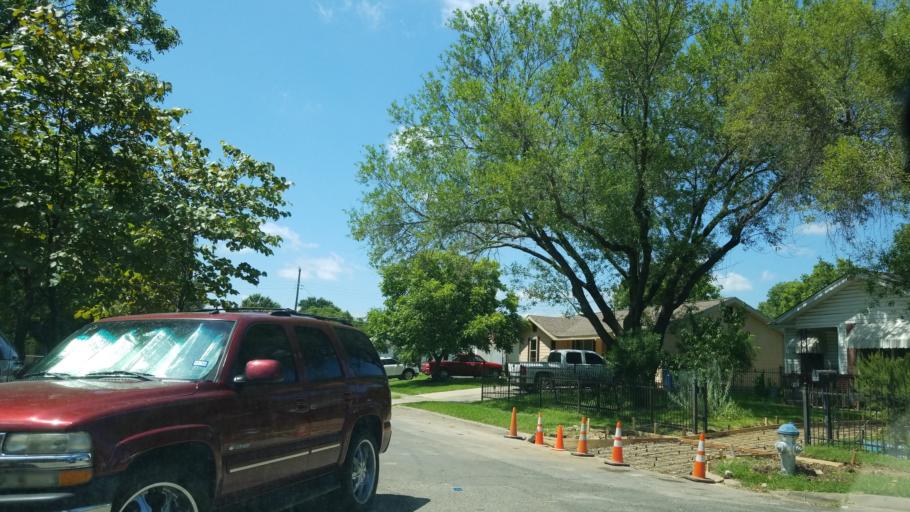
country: US
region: Texas
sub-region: Dallas County
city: Balch Springs
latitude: 32.7401
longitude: -96.6976
